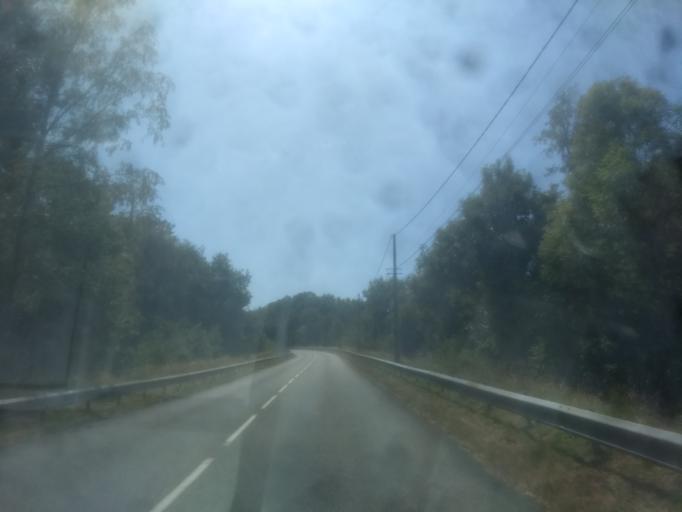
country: FR
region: Limousin
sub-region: Departement de la Haute-Vienne
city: Bessines-sur-Gartempe
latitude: 46.1019
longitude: 1.3750
